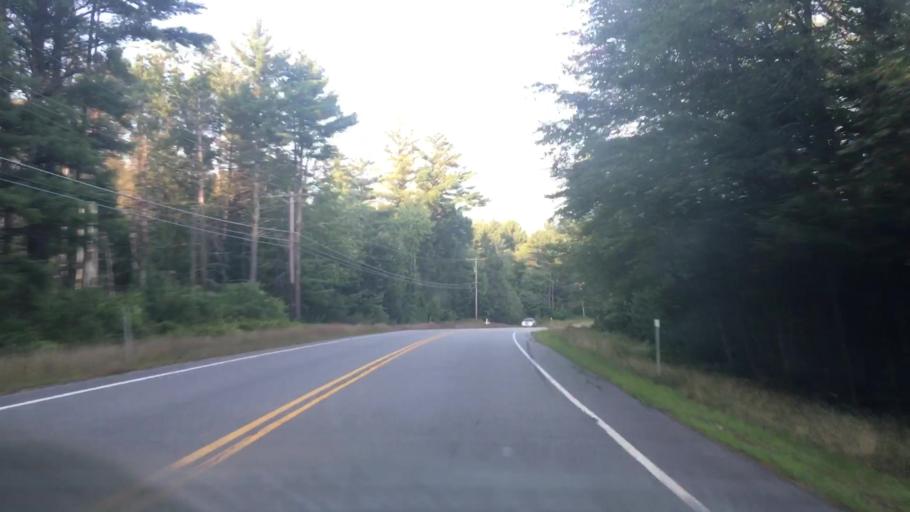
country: US
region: New Hampshire
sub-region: Belknap County
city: Gilmanton
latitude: 43.4283
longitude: -71.3492
